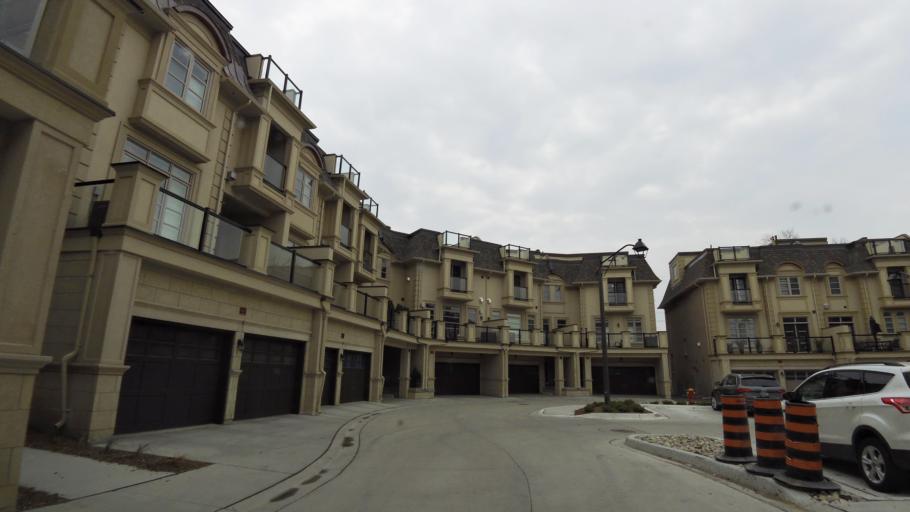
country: CA
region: Ontario
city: Oakville
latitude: 43.4369
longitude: -79.6827
